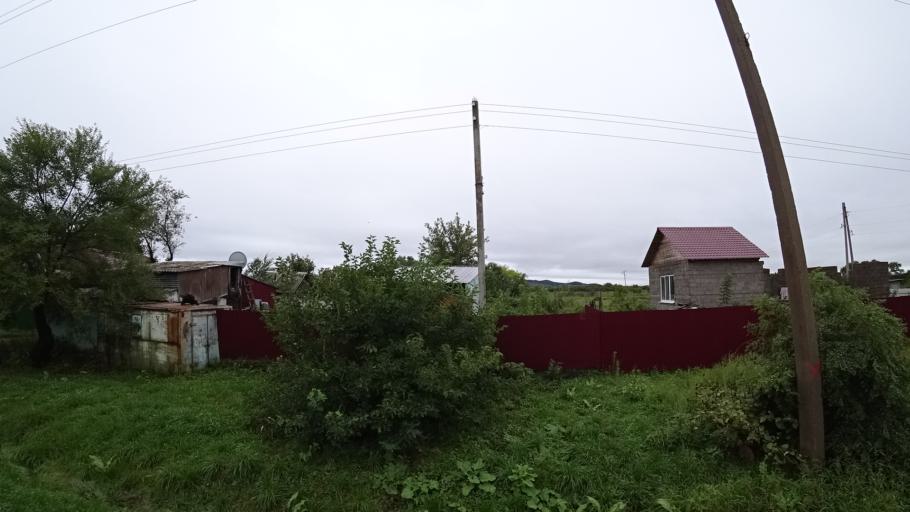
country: RU
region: Primorskiy
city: Monastyrishche
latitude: 44.1978
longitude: 132.4572
